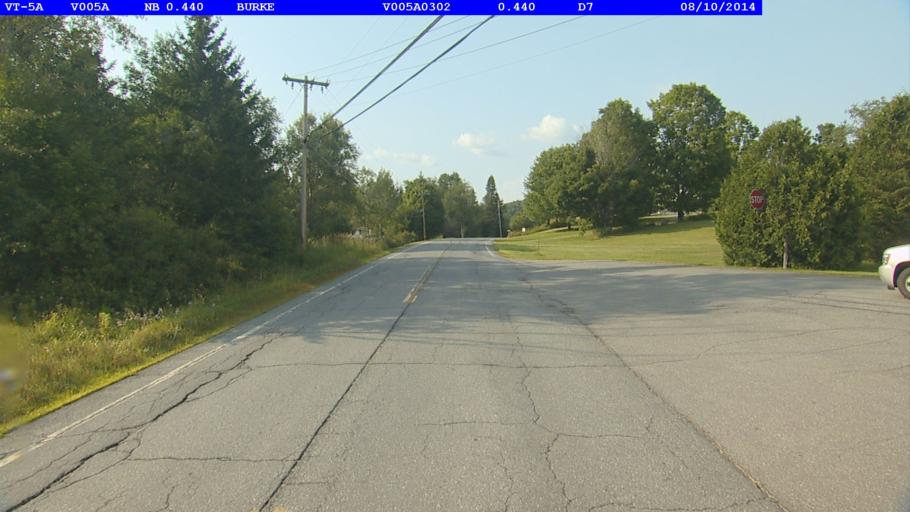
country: US
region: Vermont
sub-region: Caledonia County
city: Lyndonville
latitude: 44.6473
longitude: -71.9822
